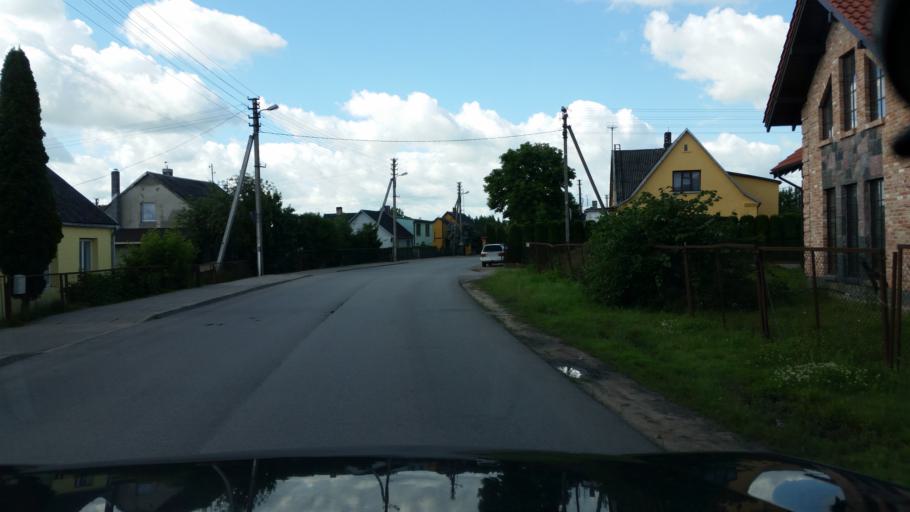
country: LT
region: Marijampoles apskritis
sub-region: Marijampole Municipality
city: Marijampole
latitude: 54.5581
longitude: 23.3413
